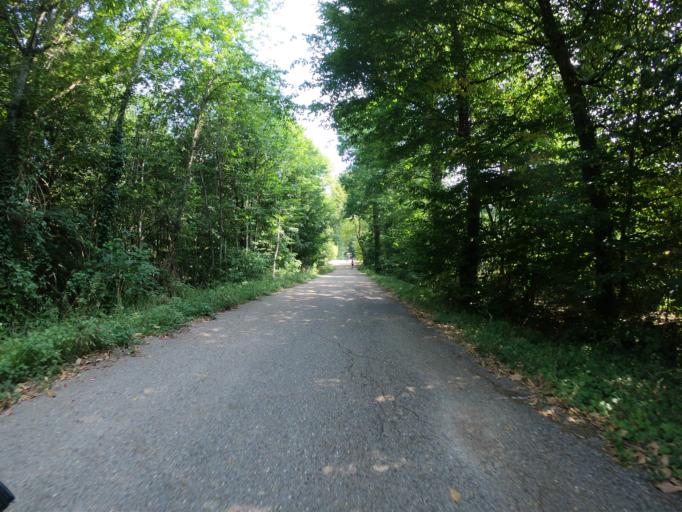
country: FR
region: Ile-de-France
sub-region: Departement de l'Essonne
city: Bievres
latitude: 48.7658
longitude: 2.2378
